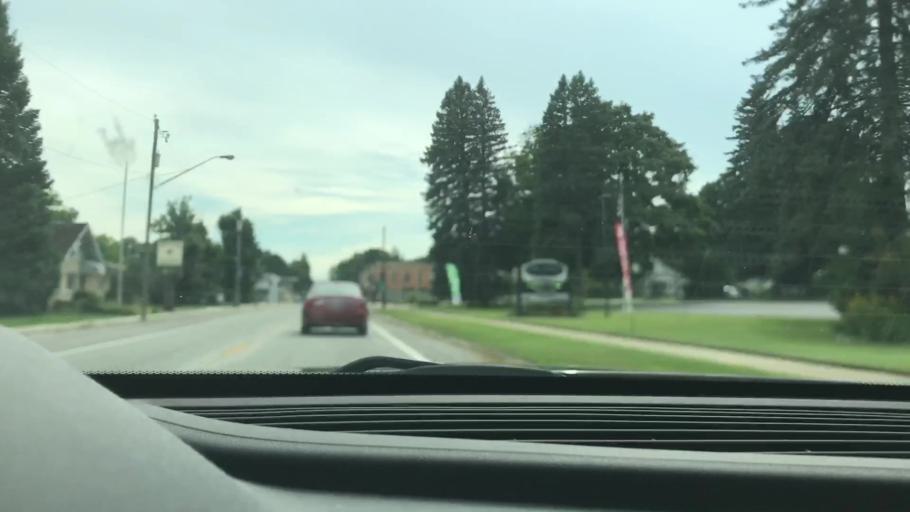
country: US
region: Michigan
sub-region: Antrim County
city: Bellaire
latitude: 45.0725
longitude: -85.2642
